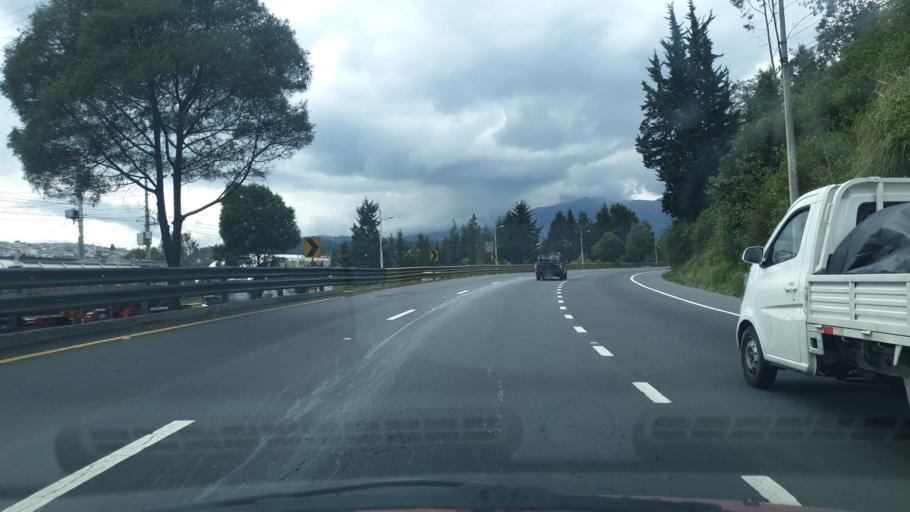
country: EC
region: Pichincha
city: Quito
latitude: -0.2467
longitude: -78.4810
